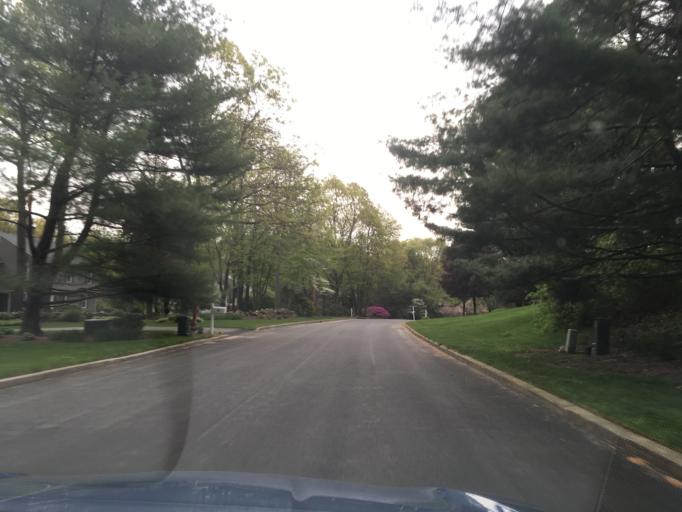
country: US
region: Rhode Island
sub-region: Kent County
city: West Warwick
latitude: 41.6589
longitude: -71.5126
